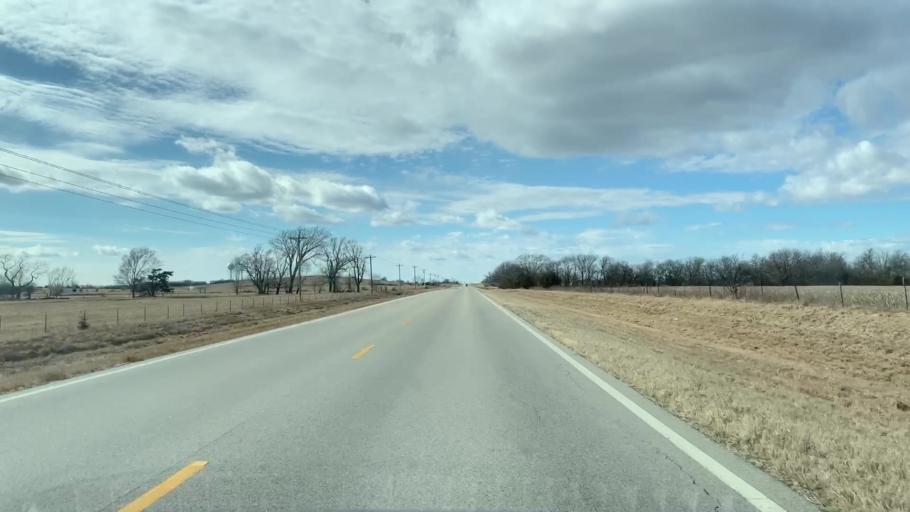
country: US
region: Kansas
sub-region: Neosho County
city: Erie
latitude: 37.5294
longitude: -95.3485
